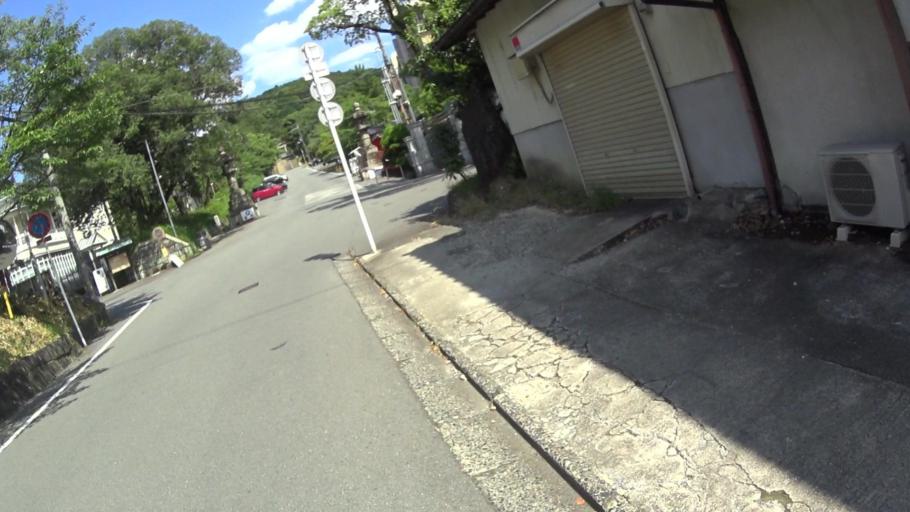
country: RU
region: Rostov
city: Remontnoye
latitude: 46.4989
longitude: 43.7785
